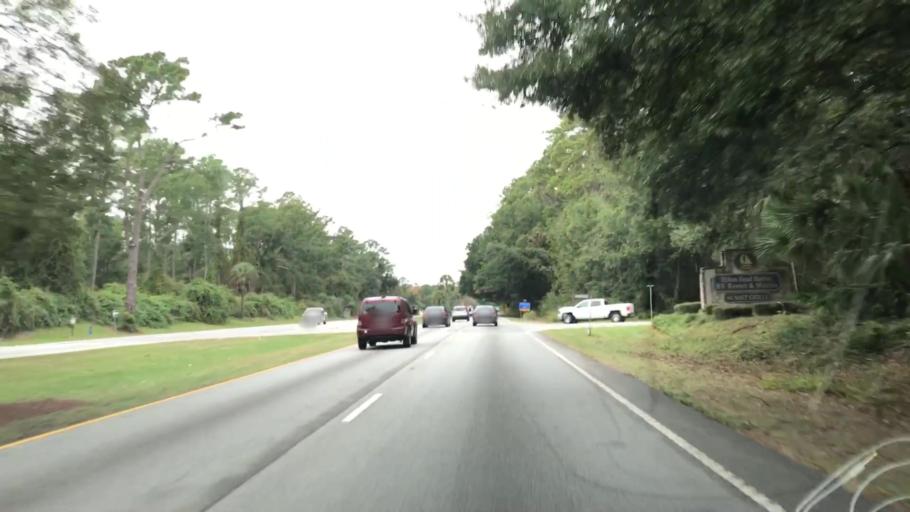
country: US
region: South Carolina
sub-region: Beaufort County
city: Hilton Head Island
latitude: 32.2184
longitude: -80.7681
